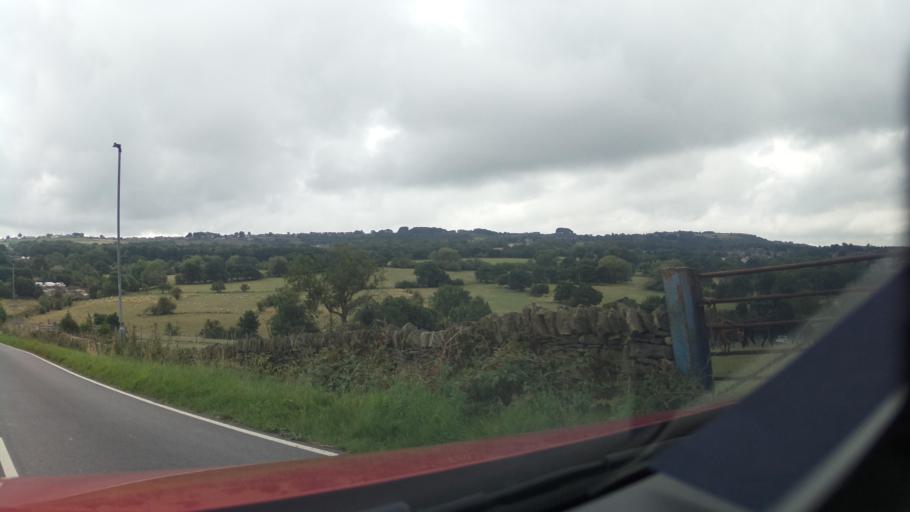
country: GB
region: England
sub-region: Kirklees
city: Shelley
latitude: 53.5949
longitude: -1.6902
